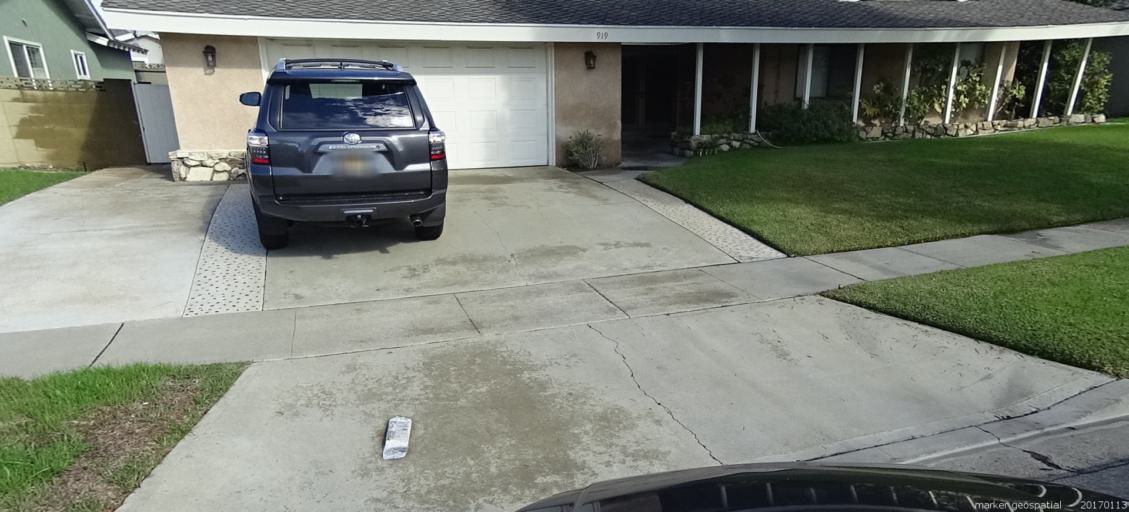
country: US
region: California
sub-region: Orange County
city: Placentia
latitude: 33.8873
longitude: -117.8477
